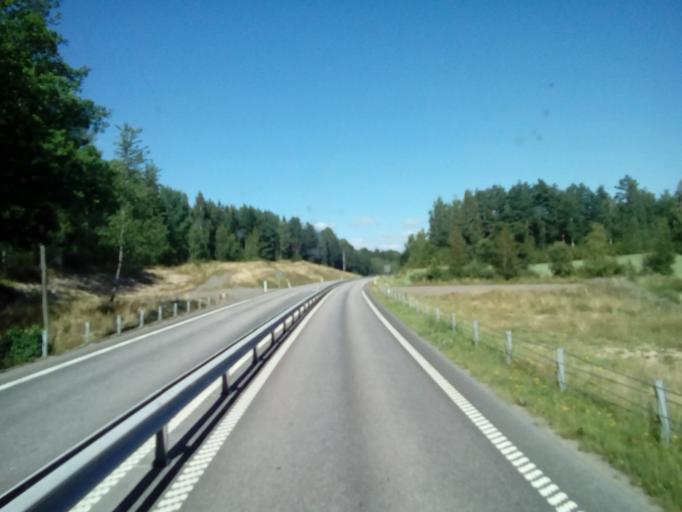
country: SE
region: OEstergoetland
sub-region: Kinda Kommun
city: Rimforsa
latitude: 58.1193
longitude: 15.6705
